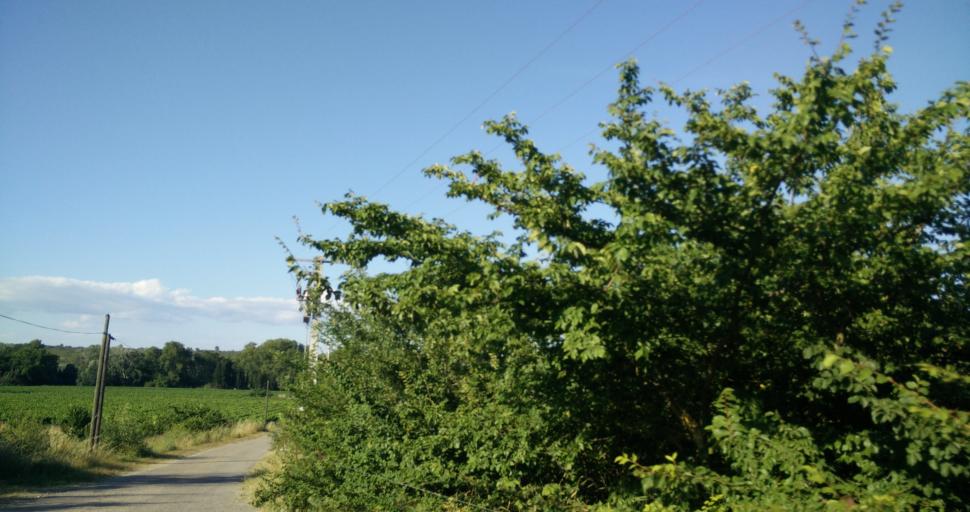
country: FR
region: Languedoc-Roussillon
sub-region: Departement de l'Herault
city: Villetelle
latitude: 43.7334
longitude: 4.1132
